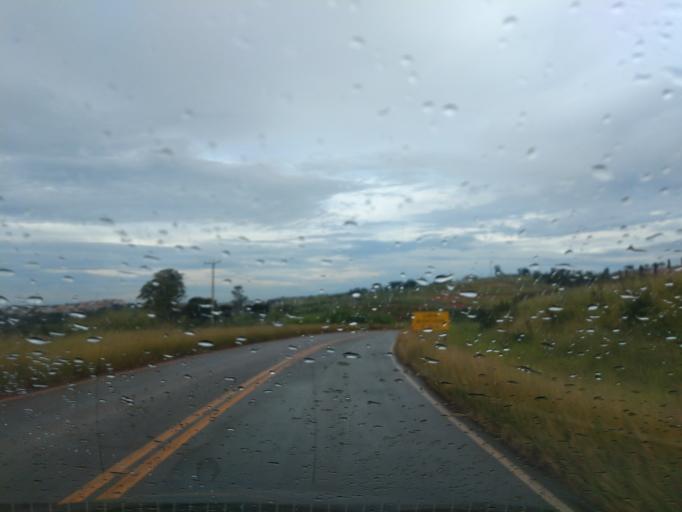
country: BR
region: Minas Gerais
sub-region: Tres Coracoes
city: Tres Coracoes
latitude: -21.7054
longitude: -45.2855
